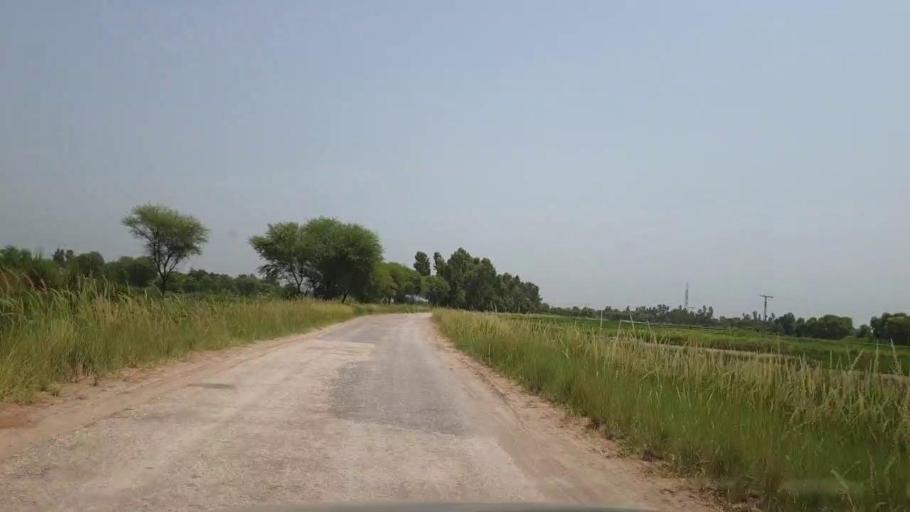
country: PK
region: Sindh
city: Ratodero
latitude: 27.8002
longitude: 68.3435
